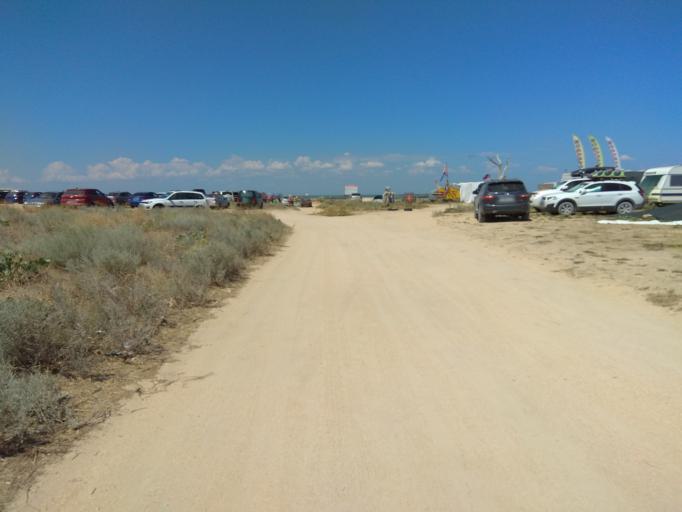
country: RU
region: Krasnodarskiy
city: Dolzhanskaya
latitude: 46.6821
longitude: 37.7374
